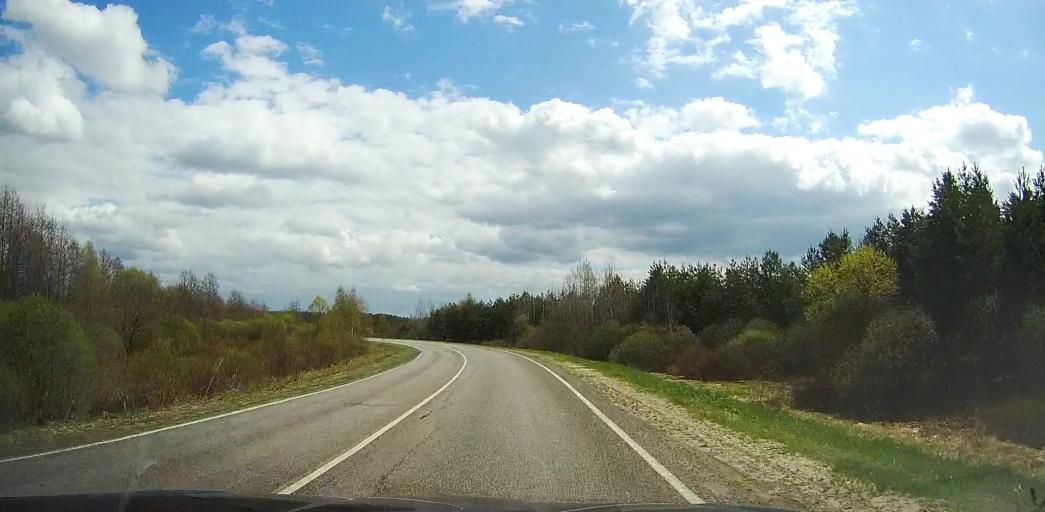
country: RU
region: Moskovskaya
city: Davydovo
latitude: 55.5477
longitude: 38.8100
